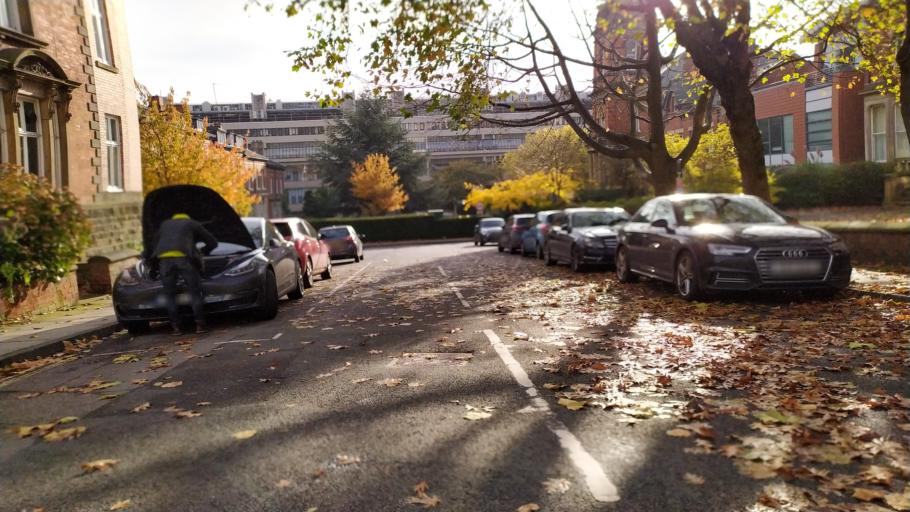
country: GB
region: England
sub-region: City and Borough of Leeds
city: Leeds
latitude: 53.8065
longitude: -1.5529
